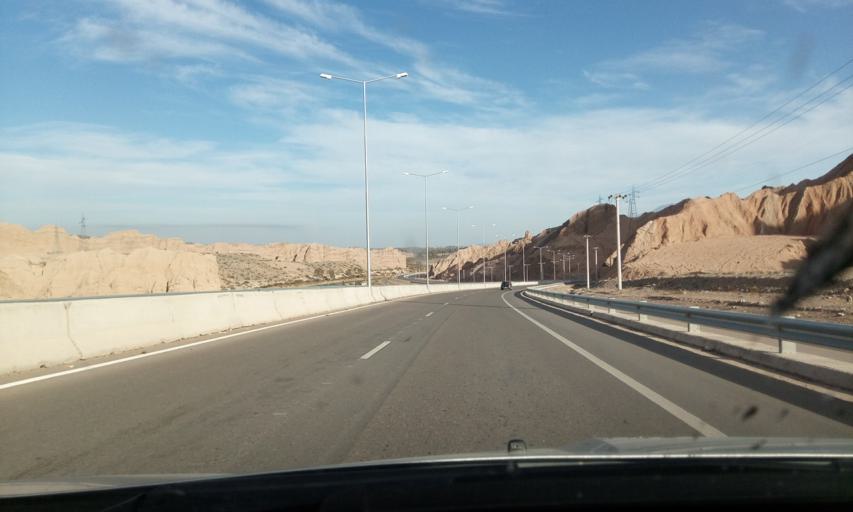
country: AR
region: San Juan
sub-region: Departamento de Rivadavia
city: Rivadavia
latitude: -31.4778
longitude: -68.6508
